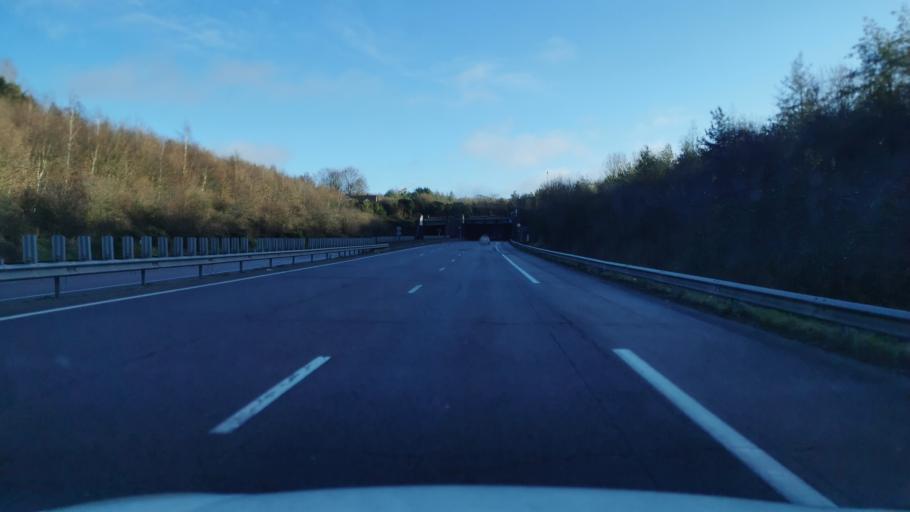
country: FR
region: Ile-de-France
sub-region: Departement des Yvelines
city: Jouars-Pontchartrain
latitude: 48.7963
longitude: 1.9048
